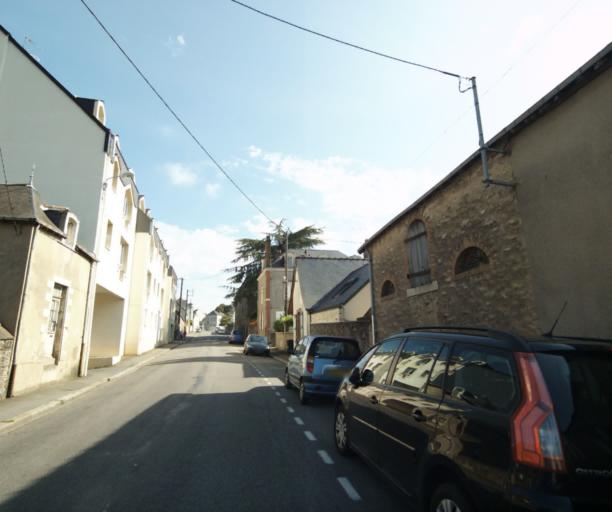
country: FR
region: Pays de la Loire
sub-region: Departement de la Mayenne
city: Laval
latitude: 48.0627
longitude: -0.7804
